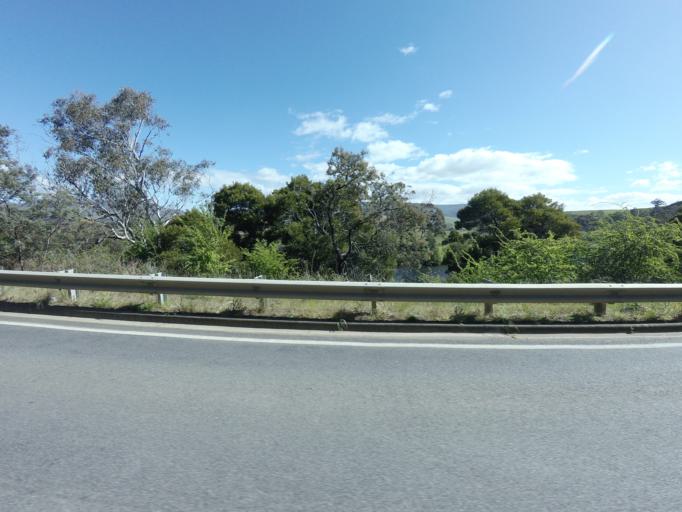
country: AU
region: Tasmania
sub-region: Derwent Valley
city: New Norfolk
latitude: -42.7334
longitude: 146.9738
